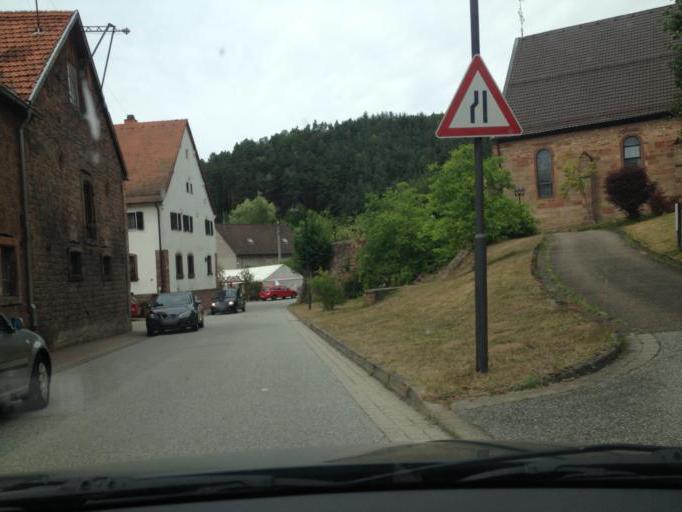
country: DE
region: Rheinland-Pfalz
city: Horbach
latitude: 49.3313
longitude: 7.6533
